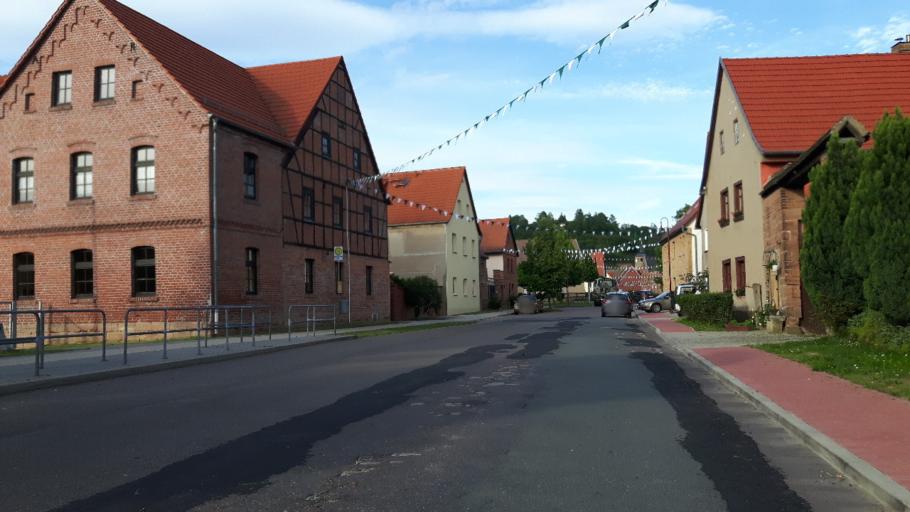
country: DE
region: Saxony-Anhalt
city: Leissling
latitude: 51.1819
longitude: 11.9076
